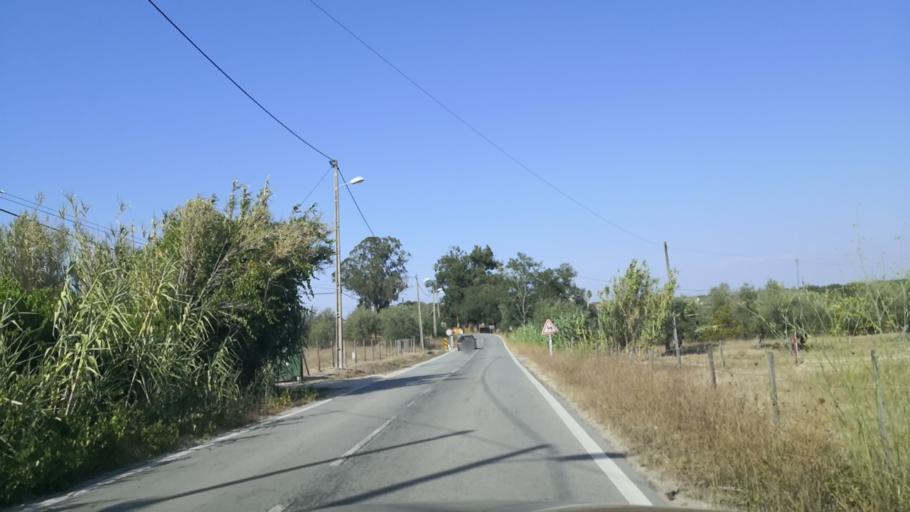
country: PT
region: Santarem
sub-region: Benavente
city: Poceirao
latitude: 38.7629
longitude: -8.6309
